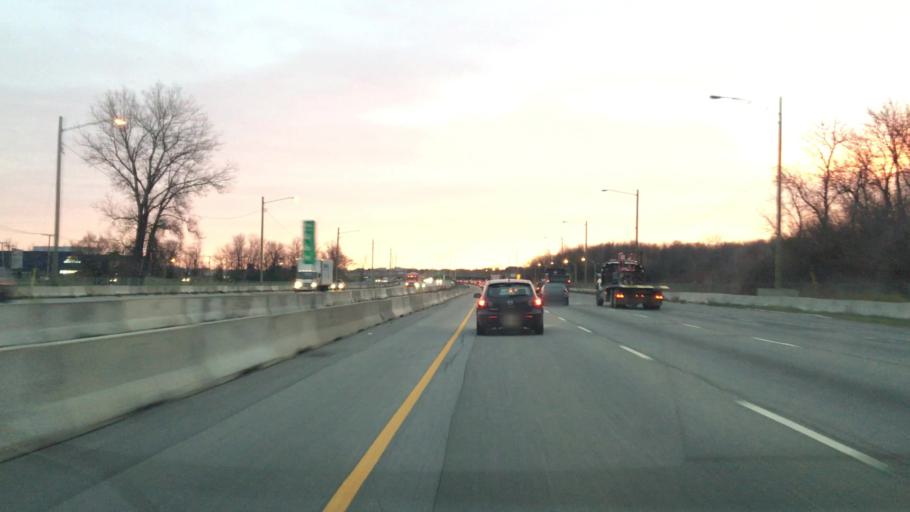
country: CA
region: Quebec
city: Beaconsfield
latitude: 45.4365
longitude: -73.8957
